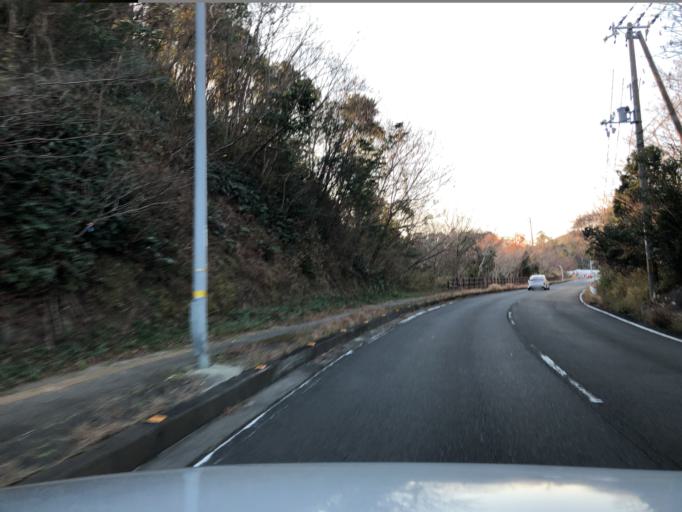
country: JP
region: Wakayama
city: Tanabe
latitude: 33.6614
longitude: 135.3761
